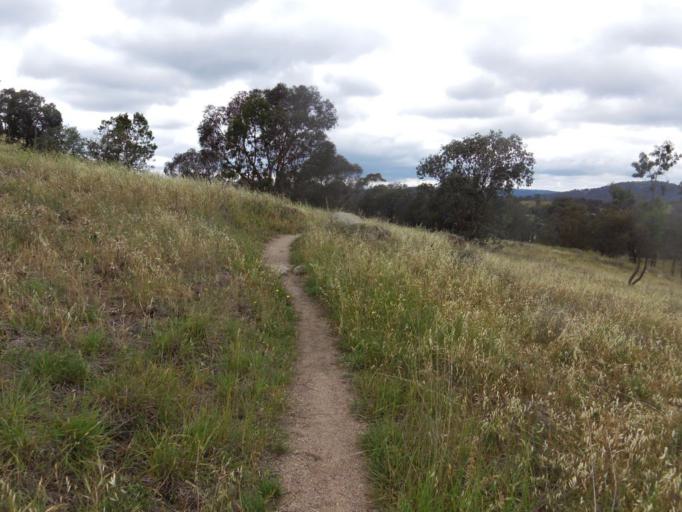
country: AU
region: Australian Capital Territory
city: Forrest
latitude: -35.3592
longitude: 149.0300
